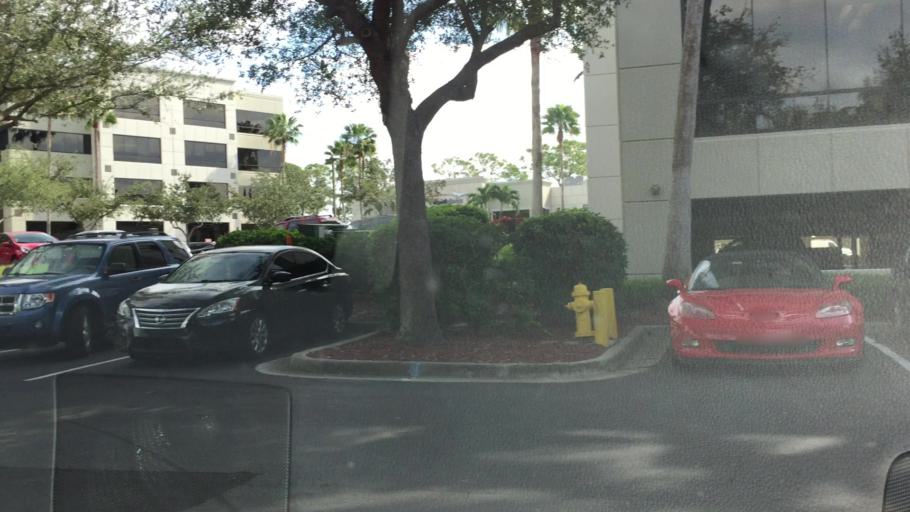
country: US
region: Florida
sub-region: Lee County
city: Bonita Springs
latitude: 26.3402
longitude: -81.8090
